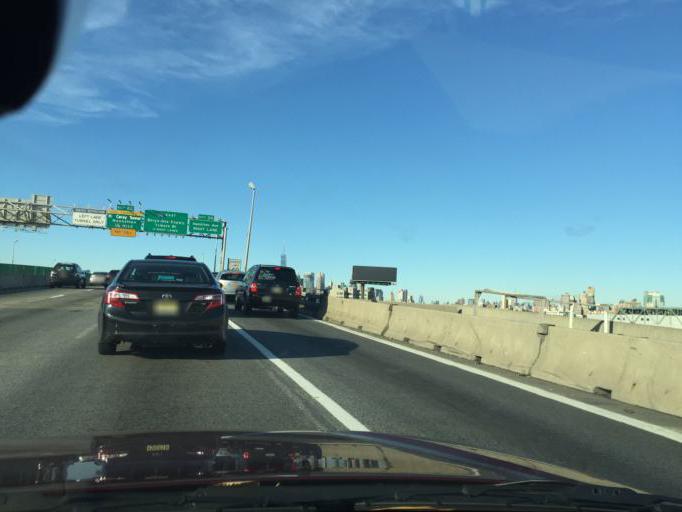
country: US
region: New York
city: New York City
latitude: 40.6710
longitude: -73.9979
